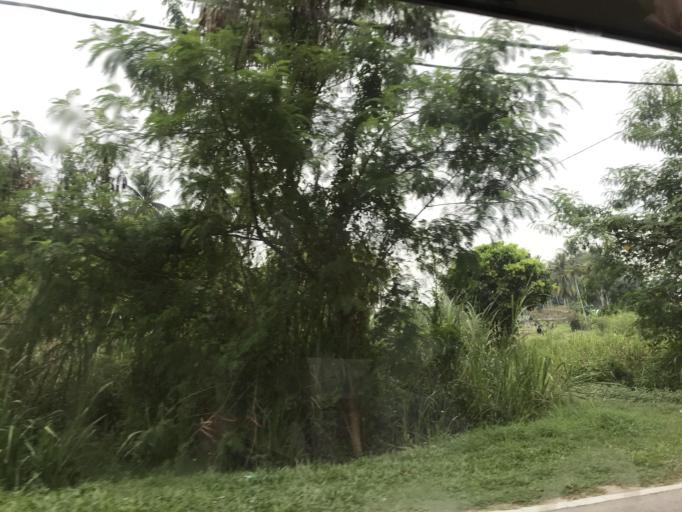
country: MY
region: Kelantan
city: Kota Bharu
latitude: 6.1761
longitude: 102.2238
